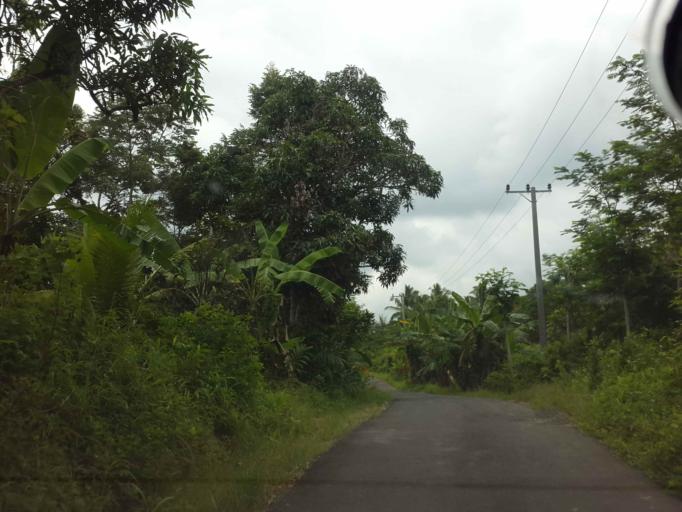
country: ID
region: Lampung
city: Sidorejo
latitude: -5.5771
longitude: 105.4829
